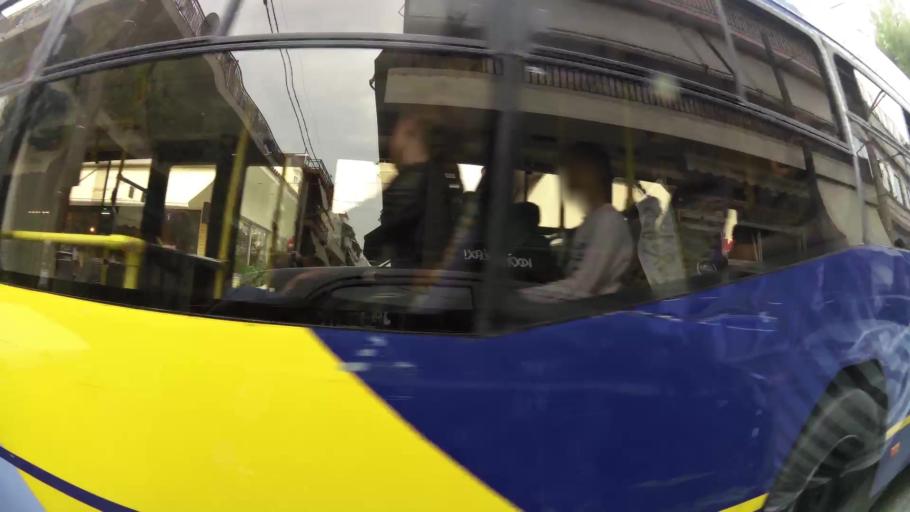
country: GR
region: Attica
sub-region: Nomos Piraios
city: Agios Ioannis Rentis
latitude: 37.9563
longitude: 23.6616
